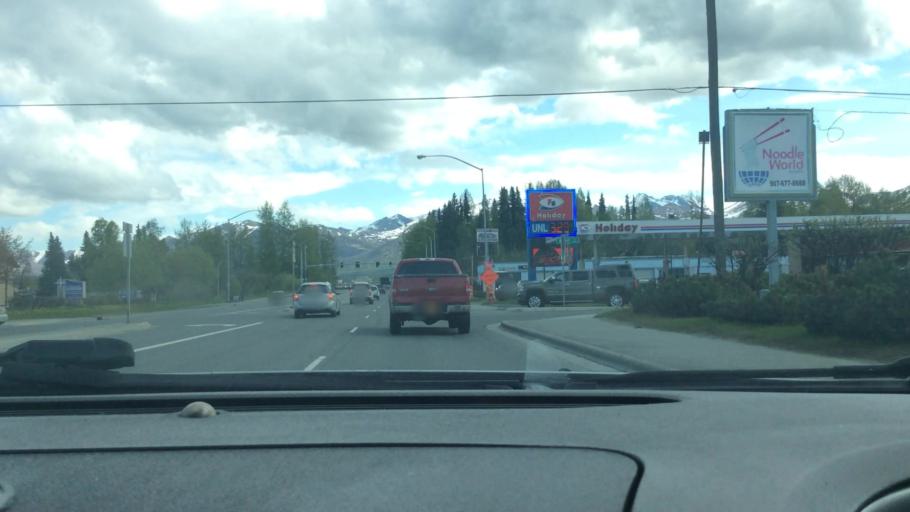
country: US
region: Alaska
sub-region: Anchorage Municipality
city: Anchorage
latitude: 61.1808
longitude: -149.8277
